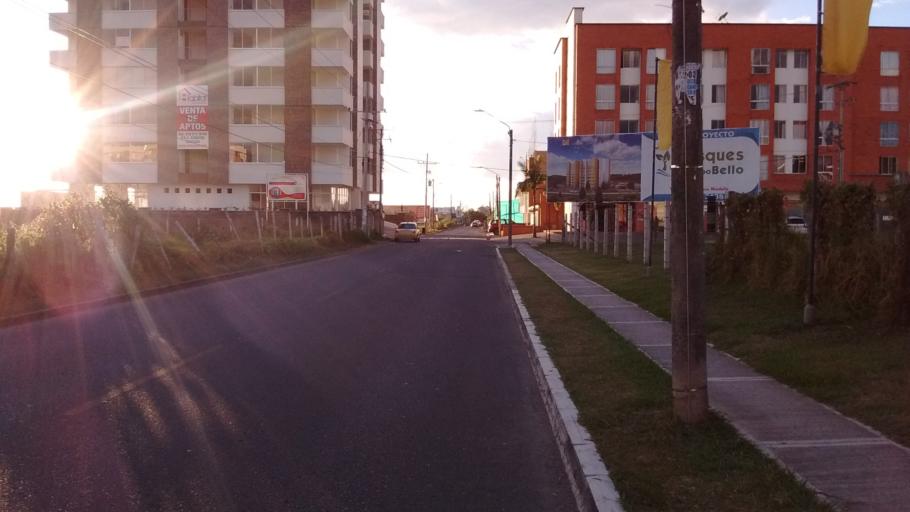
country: CO
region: Cauca
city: Popayan
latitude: 2.4674
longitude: -76.5895
